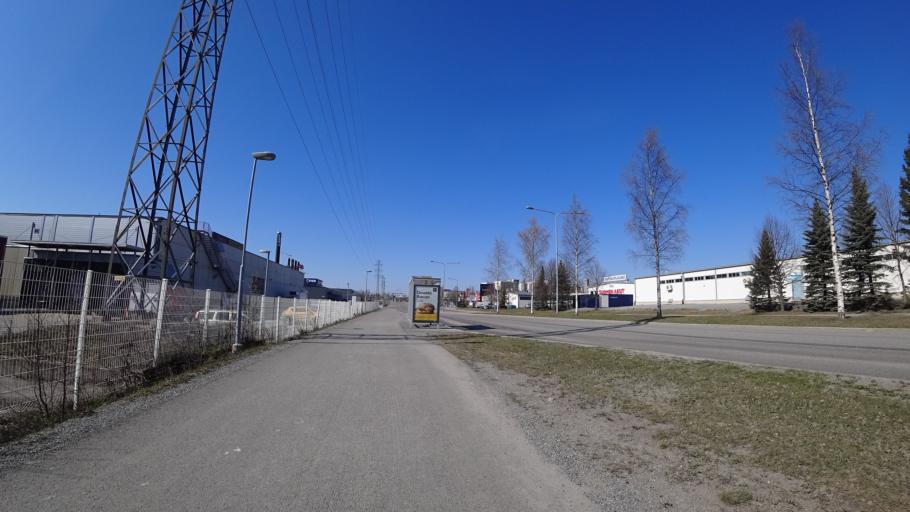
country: FI
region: Pirkanmaa
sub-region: Tampere
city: Pirkkala
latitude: 61.5157
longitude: 23.6708
